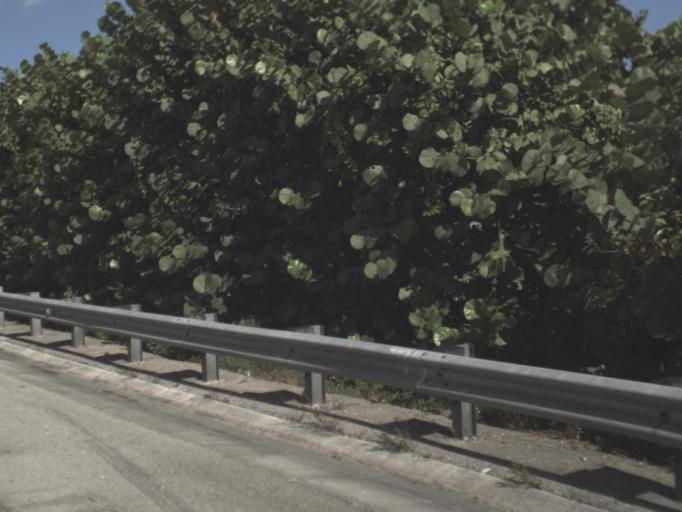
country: US
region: Florida
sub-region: Broward County
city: Miramar
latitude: 25.9937
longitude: -80.2254
